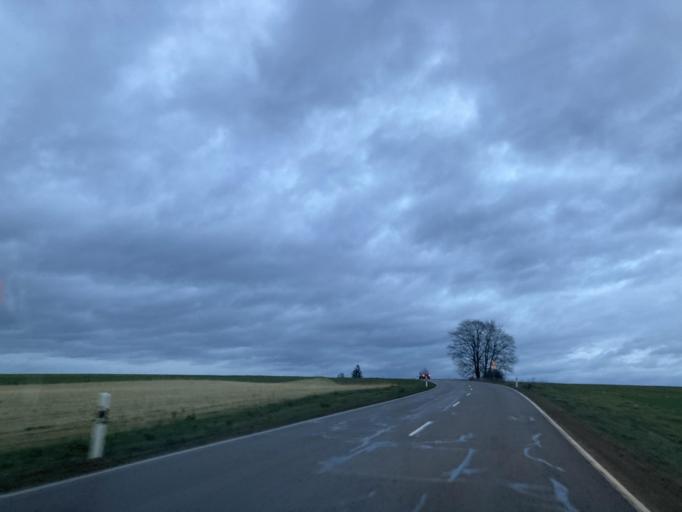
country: DE
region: Baden-Wuerttemberg
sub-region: Tuebingen Region
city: Rammingen
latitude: 48.5244
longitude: 10.1783
